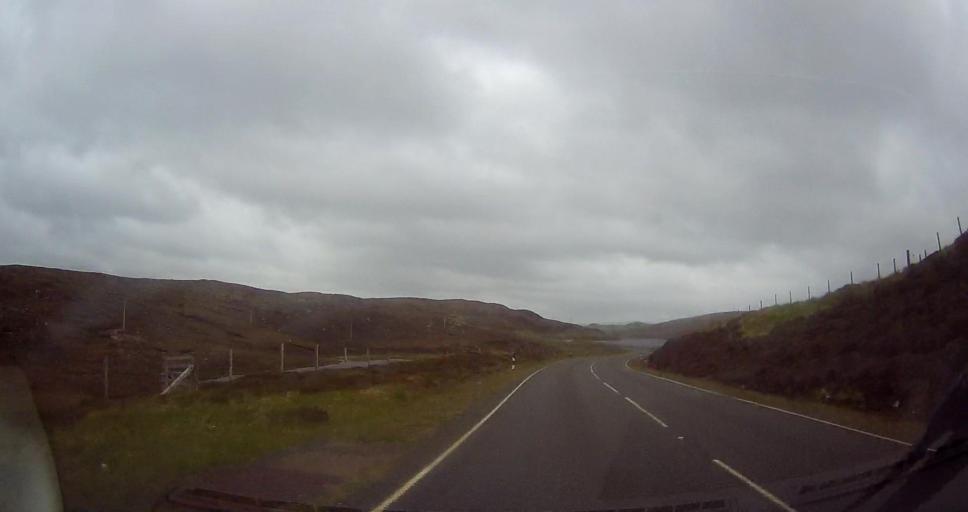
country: GB
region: Scotland
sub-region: Shetland Islands
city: Lerwick
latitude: 60.4493
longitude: -1.3957
